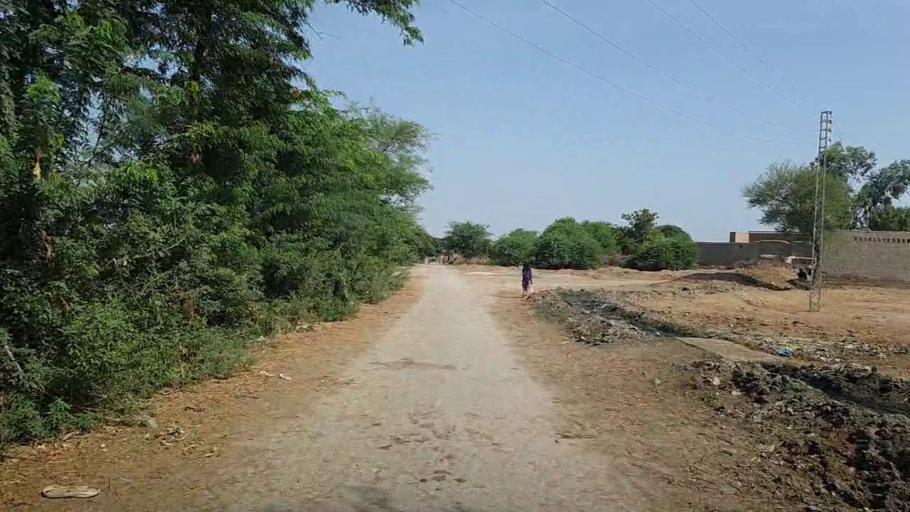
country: PK
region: Sindh
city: Mehar
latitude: 27.1176
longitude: 67.8414
